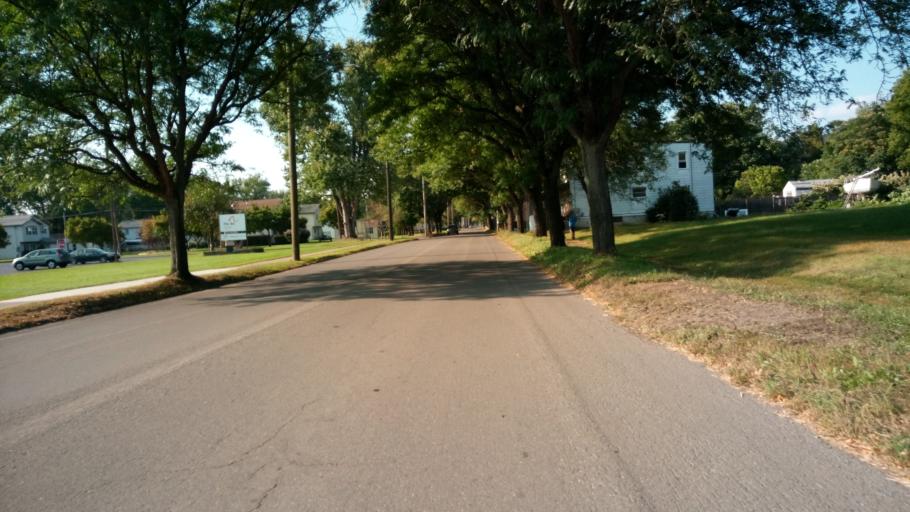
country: US
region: New York
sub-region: Chemung County
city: Elmira
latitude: 42.0993
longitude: -76.7968
